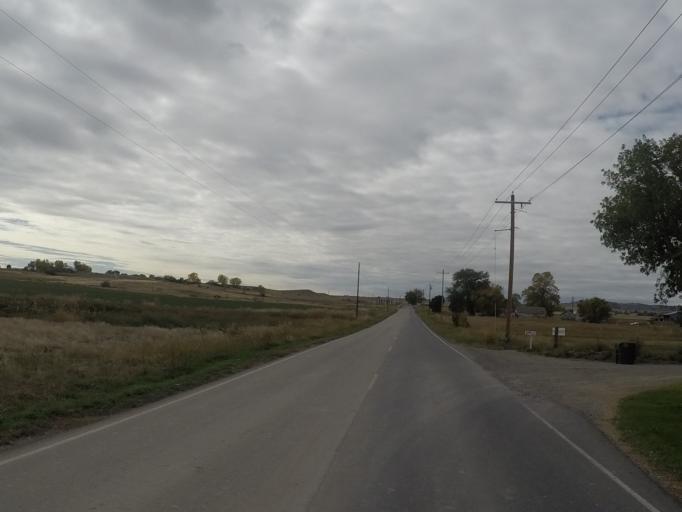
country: US
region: Montana
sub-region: Yellowstone County
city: Laurel
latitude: 45.7696
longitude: -108.6721
